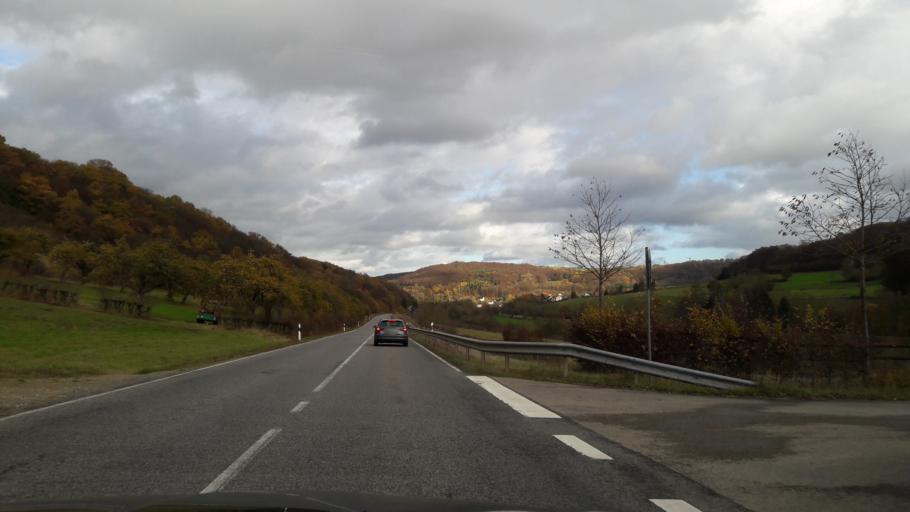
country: DE
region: Rheinland-Pfalz
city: Echternacherbruck
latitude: 49.8134
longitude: 6.4549
